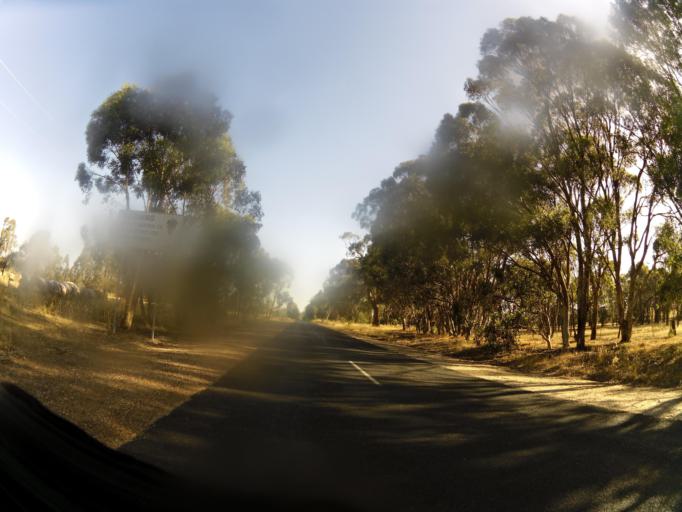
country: AU
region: Victoria
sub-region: Murrindindi
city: Kinglake West
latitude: -36.9916
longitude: 145.1124
